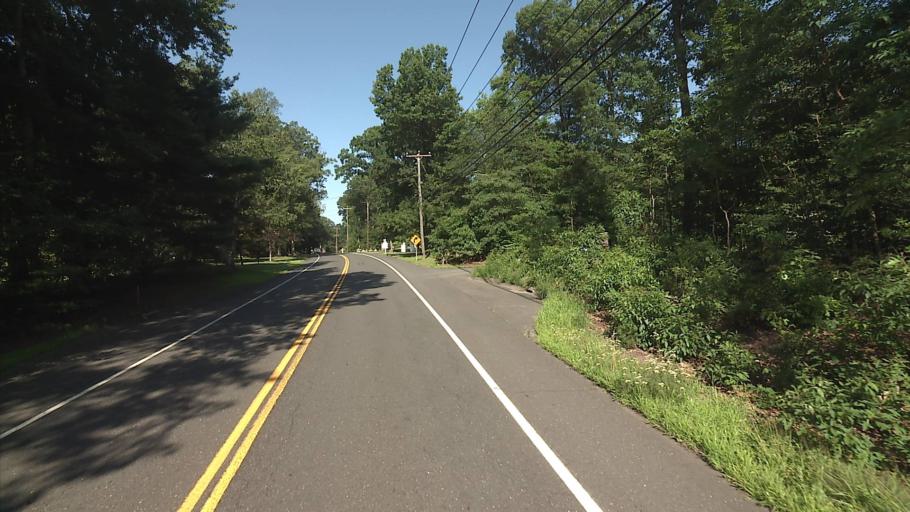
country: US
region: Connecticut
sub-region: Hartford County
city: Salmon Brook
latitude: 41.9553
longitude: -72.8256
